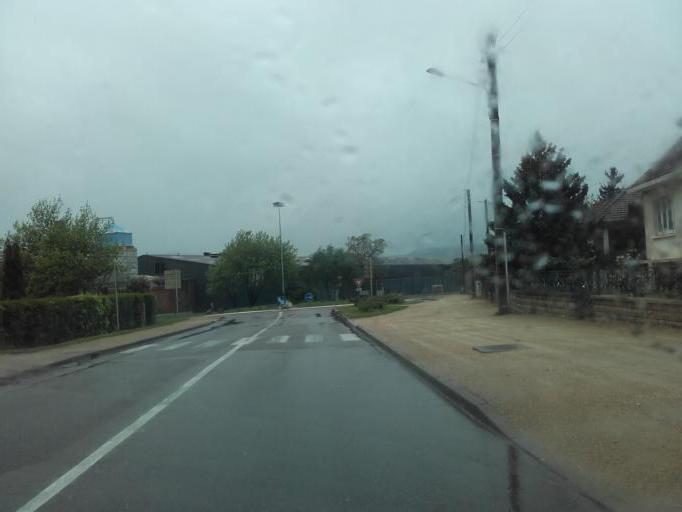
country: FR
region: Bourgogne
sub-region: Departement de Saone-et-Loire
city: Chagny
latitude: 46.9037
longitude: 4.7569
